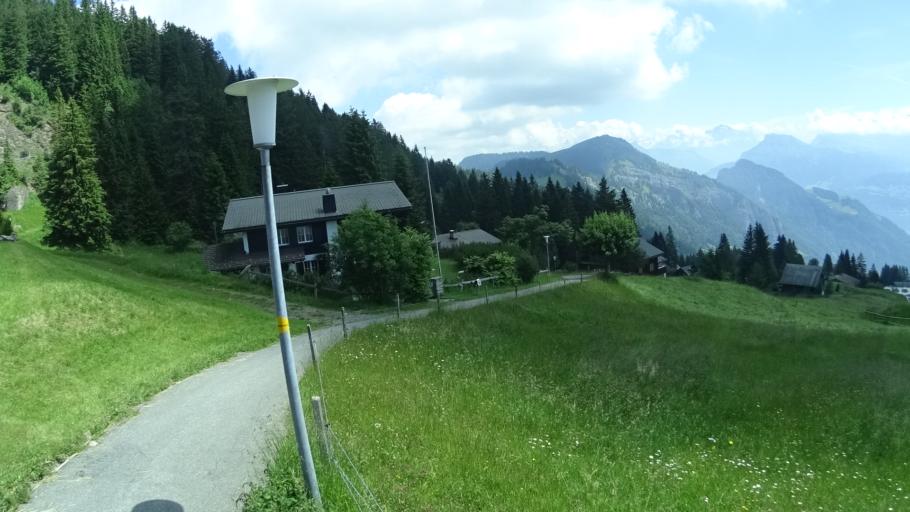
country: CH
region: Lucerne
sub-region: Lucerne-Land District
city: Weggis
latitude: 47.0475
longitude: 8.4639
